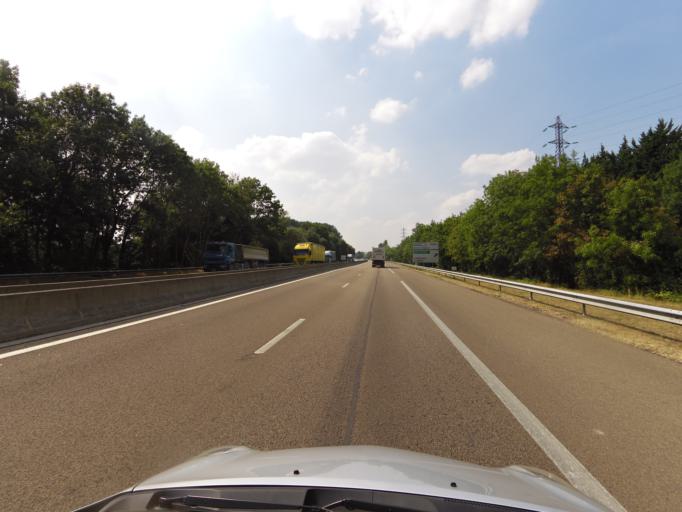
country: FR
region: Champagne-Ardenne
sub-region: Departement de la Marne
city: Tinqueux
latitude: 49.2558
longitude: 3.9921
